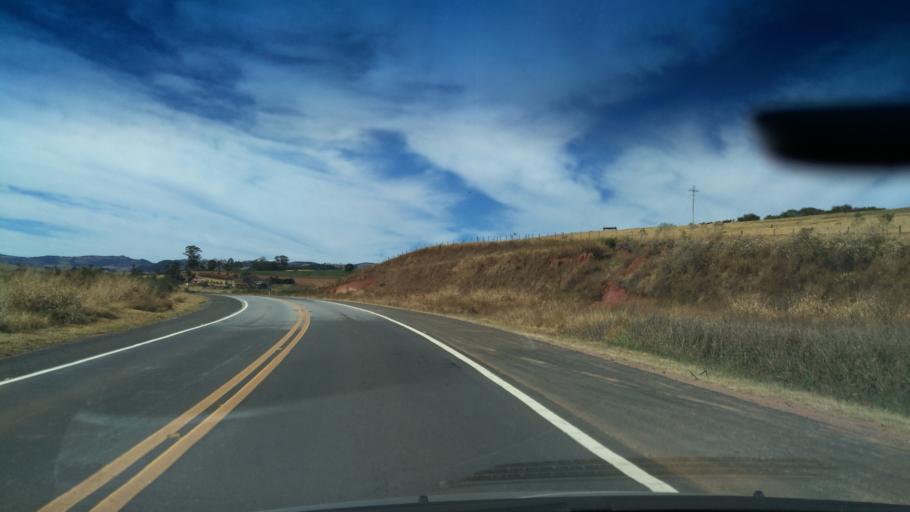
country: BR
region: Minas Gerais
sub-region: Borda Da Mata
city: Borda da Mata
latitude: -22.0547
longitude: -46.2885
